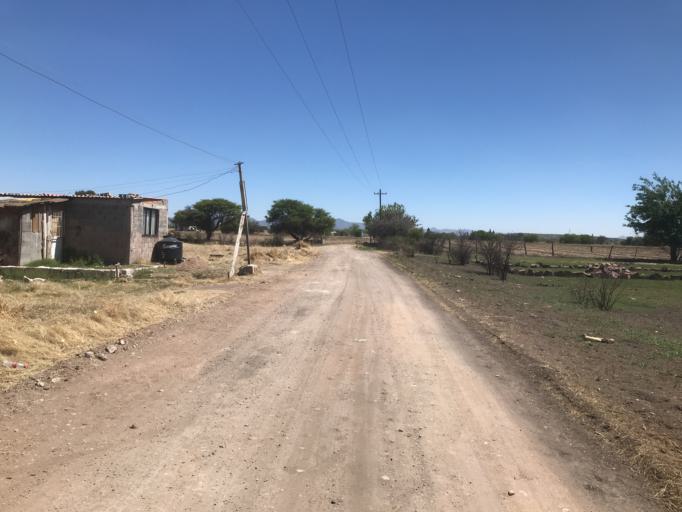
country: MX
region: Durango
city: Victoria de Durango
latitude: 24.0830
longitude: -104.5706
